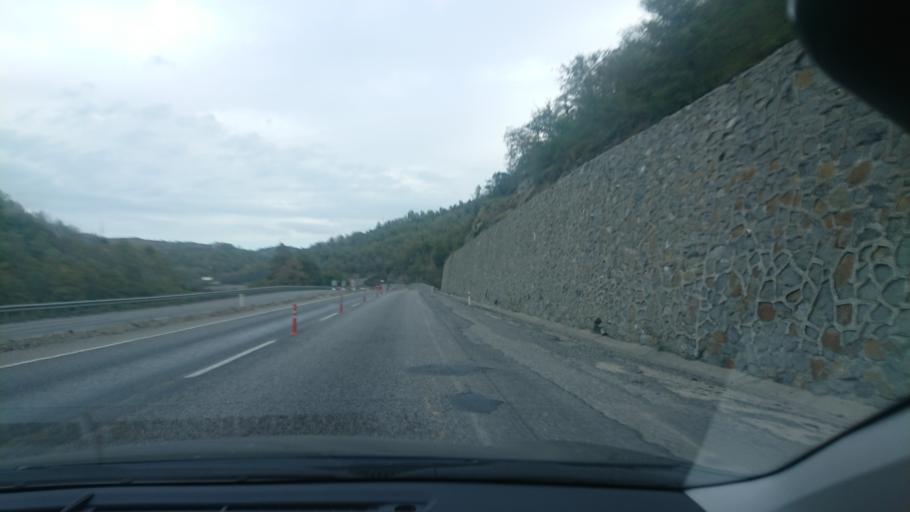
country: TR
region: Zonguldak
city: Beycuma
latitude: 41.4021
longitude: 31.9373
